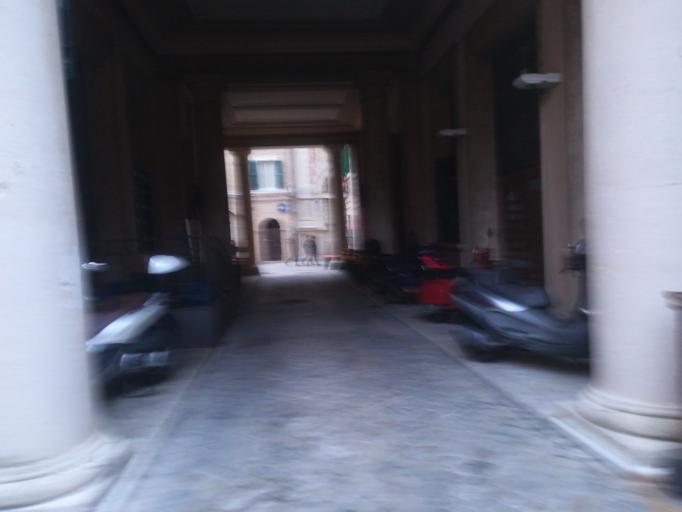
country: IT
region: The Marches
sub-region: Provincia di Macerata
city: Macerata
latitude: 43.3001
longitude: 13.4514
